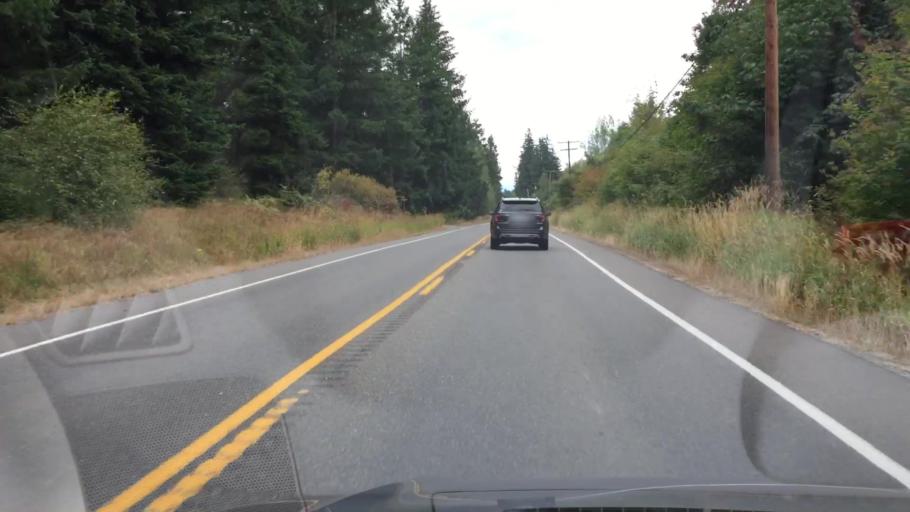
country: US
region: Washington
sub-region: Pierce County
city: Graham
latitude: 46.9908
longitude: -122.2963
